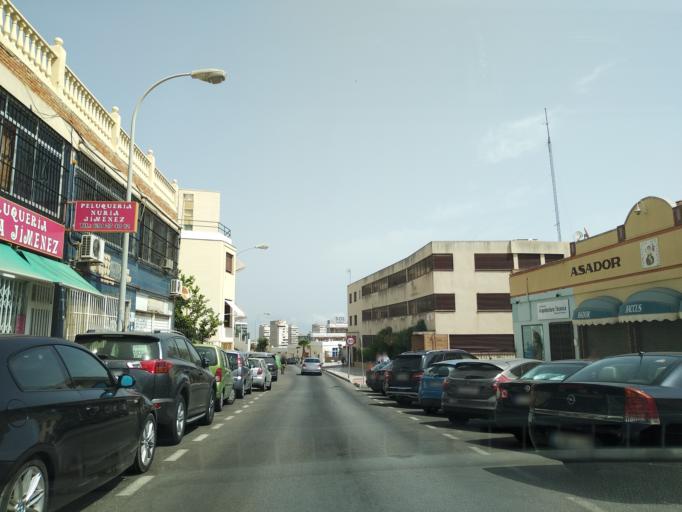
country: ES
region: Andalusia
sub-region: Provincia de Malaga
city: Torremolinos
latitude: 36.6240
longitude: -4.4964
